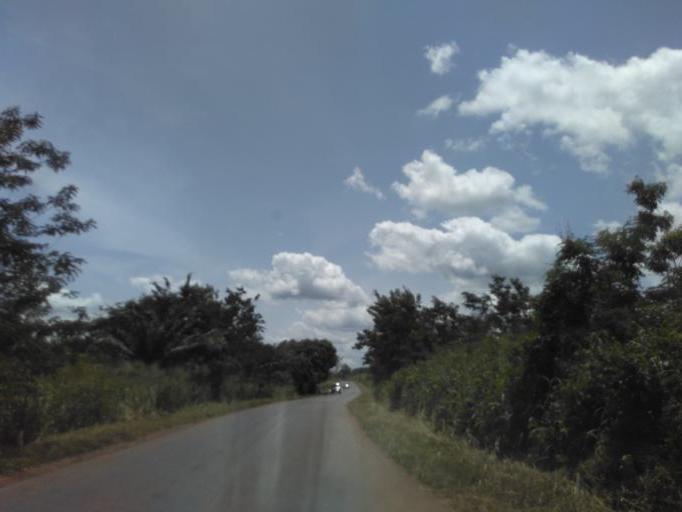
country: GH
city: Akropong
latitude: 6.0440
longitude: -0.0912
